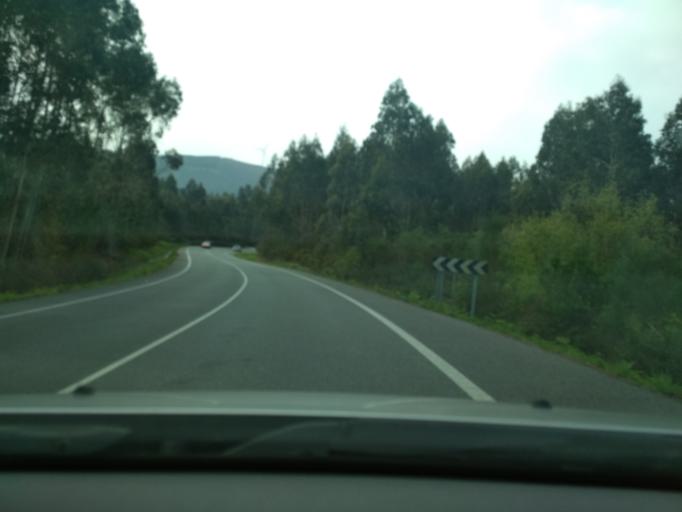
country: ES
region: Galicia
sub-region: Provincia de Pontevedra
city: Catoira
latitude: 42.6590
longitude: -8.7037
